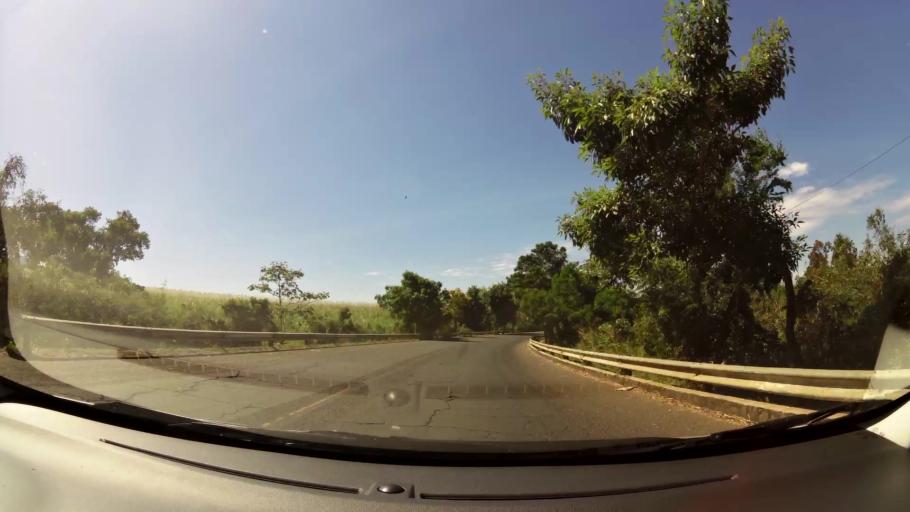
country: SV
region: Ahuachapan
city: Ahuachapan
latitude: 13.9365
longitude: -89.8495
